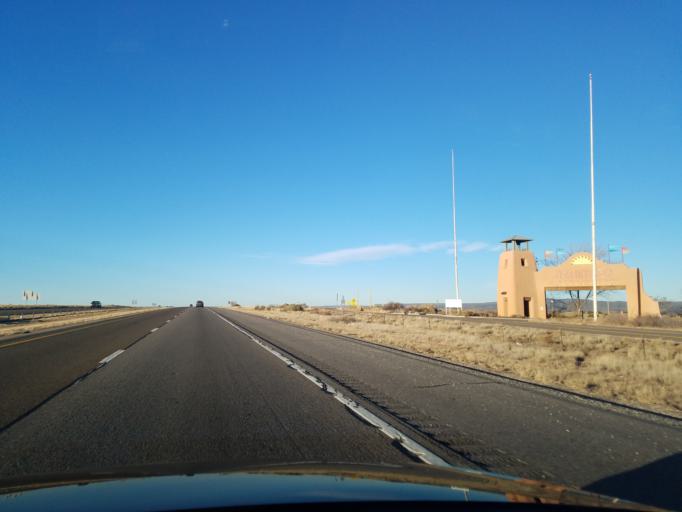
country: US
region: New Mexico
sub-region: Sandoval County
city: Santo Domingo Pueblo
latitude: 35.4534
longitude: -106.3458
